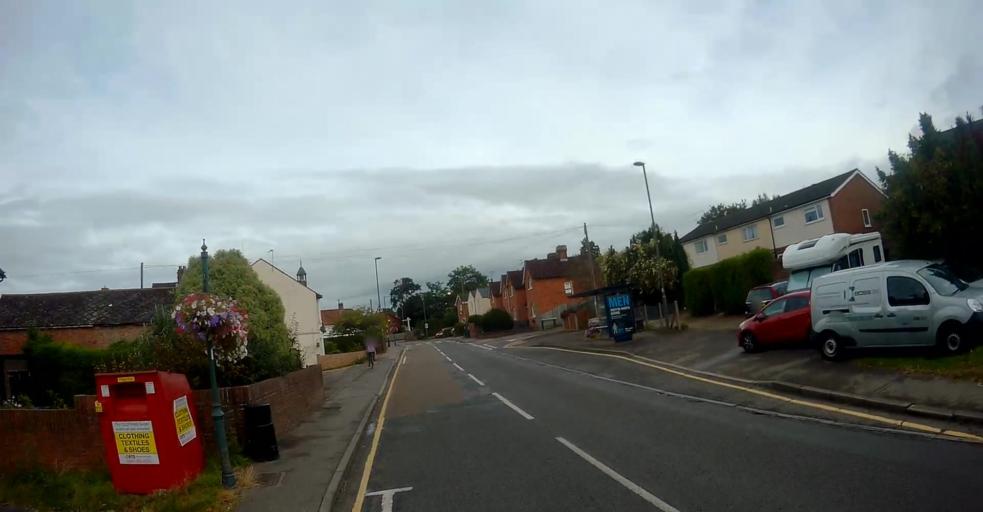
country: GB
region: England
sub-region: Surrey
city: Pirbright
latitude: 51.3046
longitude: -0.6383
